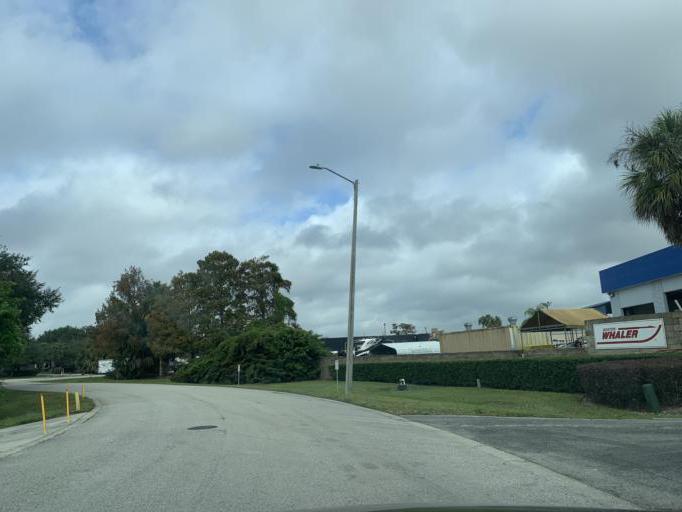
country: US
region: Florida
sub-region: Orange County
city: Eatonville
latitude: 28.6129
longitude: -81.3879
